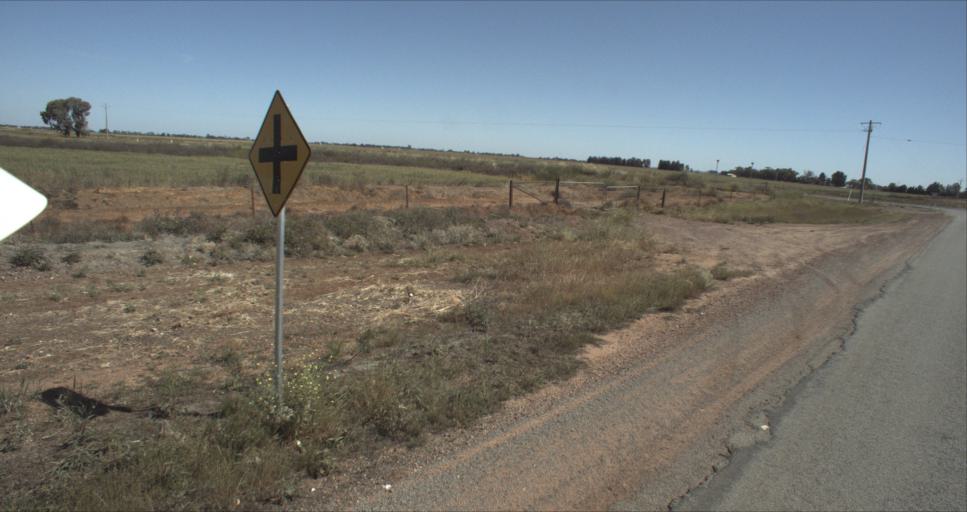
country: AU
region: New South Wales
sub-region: Leeton
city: Leeton
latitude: -34.5510
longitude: 146.3146
